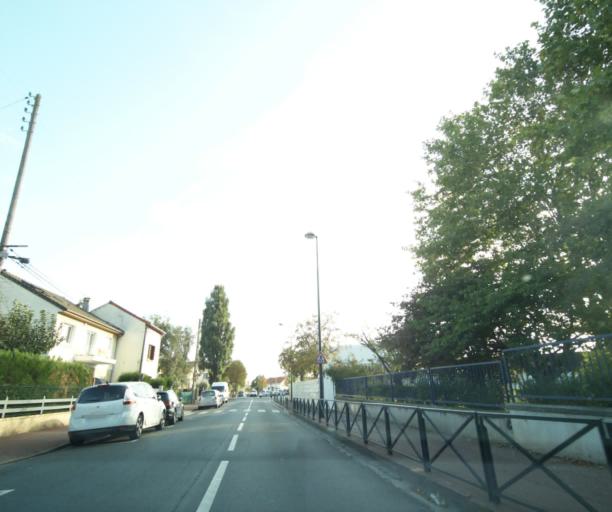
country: FR
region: Ile-de-France
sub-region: Departement de l'Essonne
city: Bievres
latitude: 48.7821
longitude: 2.2337
